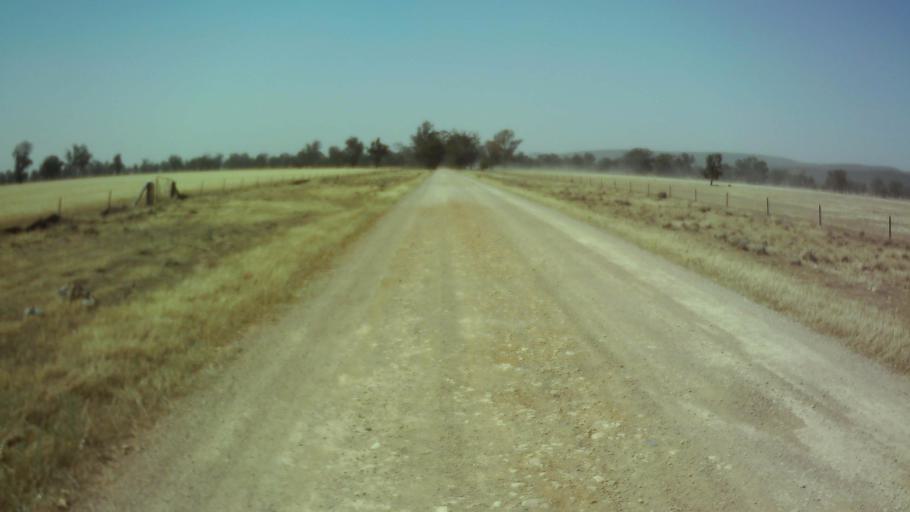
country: AU
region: New South Wales
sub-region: Weddin
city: Grenfell
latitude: -34.0066
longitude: 147.9171
